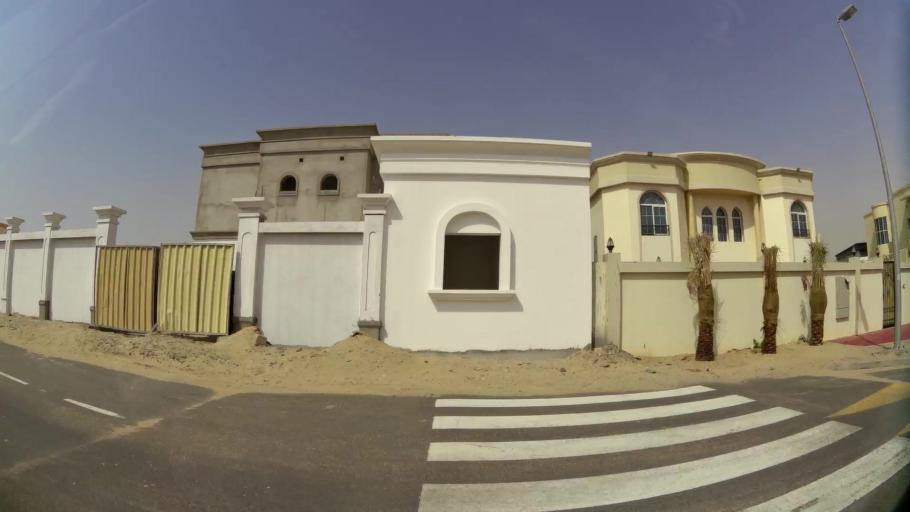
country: AE
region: Ash Shariqah
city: Sharjah
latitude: 25.2586
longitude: 55.4681
